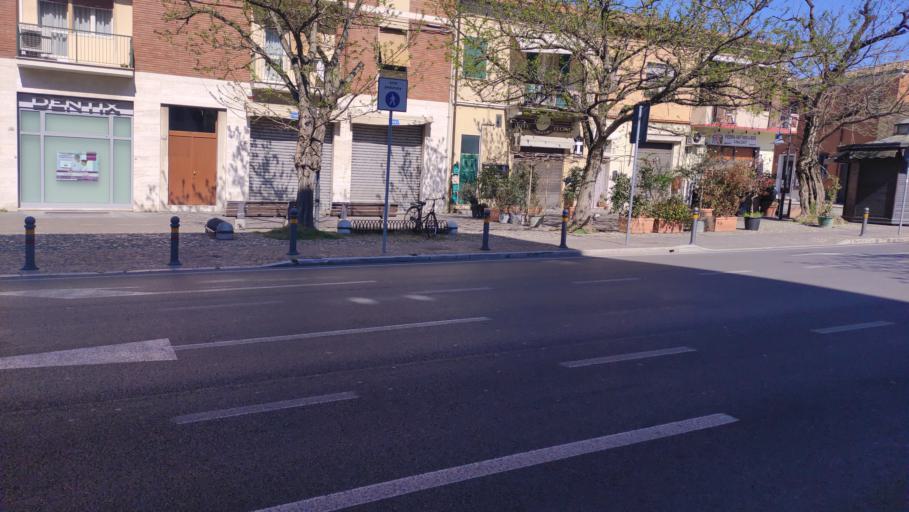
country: IT
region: Emilia-Romagna
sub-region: Provincia di Ravenna
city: Ravenna
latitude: 44.4199
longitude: 12.1937
